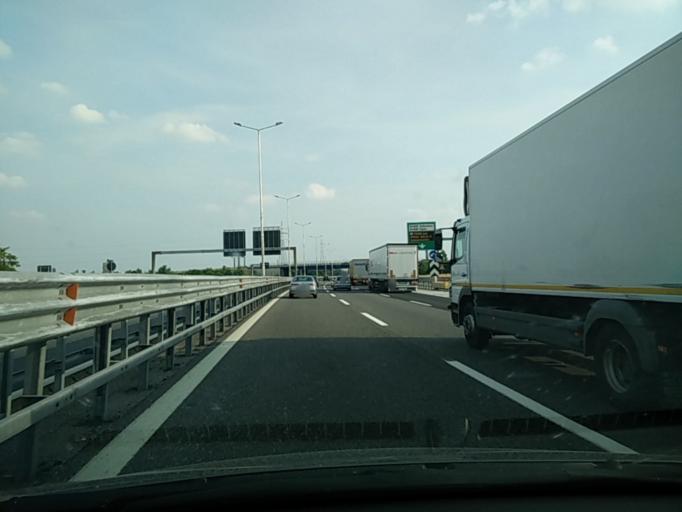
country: IT
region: Lombardy
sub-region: Citta metropolitana di Milano
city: Figino
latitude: 45.5006
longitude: 9.0667
